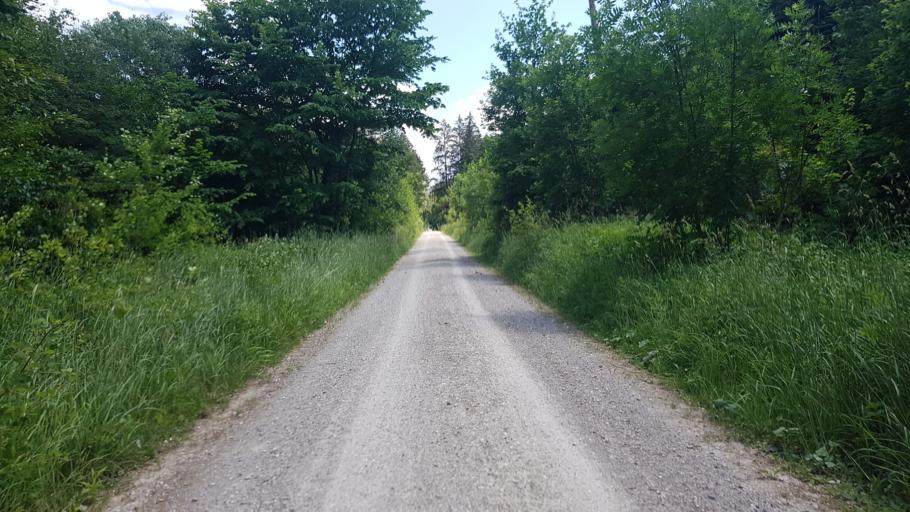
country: DE
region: Bavaria
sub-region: Upper Bavaria
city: Planegg
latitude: 48.0509
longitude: 11.4324
